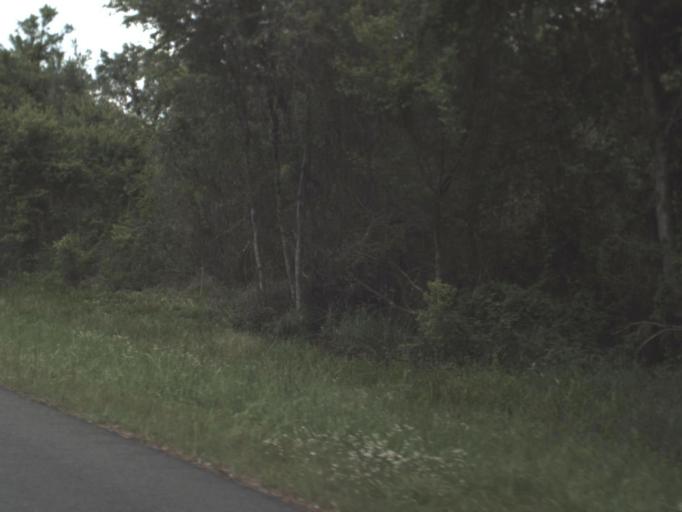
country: US
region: Florida
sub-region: Hamilton County
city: Jasper
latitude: 30.5307
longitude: -82.6757
